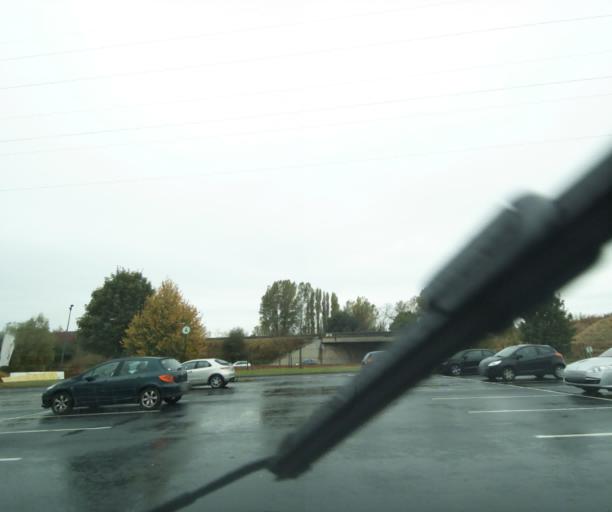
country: FR
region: Nord-Pas-de-Calais
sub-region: Departement du Nord
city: Roncq
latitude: 50.7375
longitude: 3.1330
